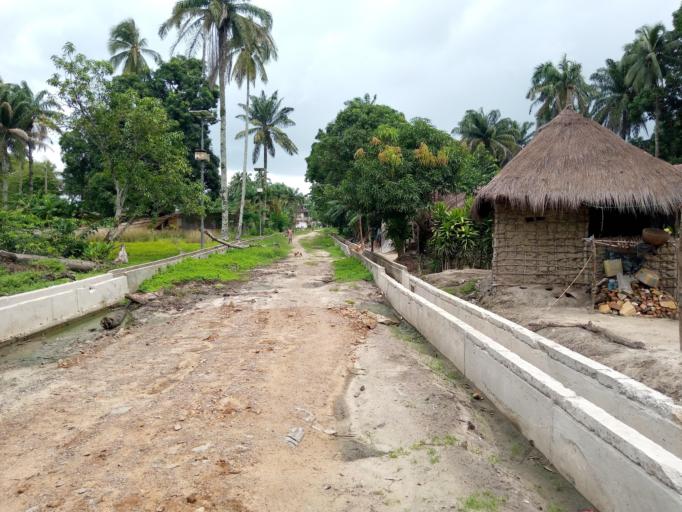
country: SL
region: Southern Province
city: Bonthe
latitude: 7.5343
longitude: -12.5041
